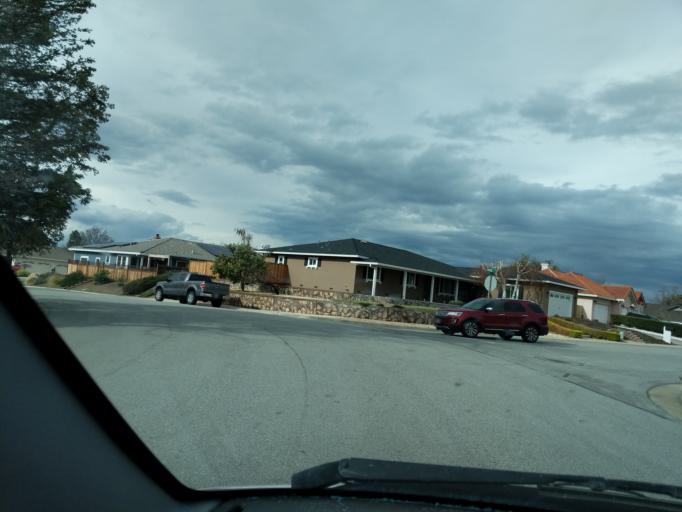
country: US
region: California
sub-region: San Benito County
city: Ridgemark
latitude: 36.8091
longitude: -121.3549
